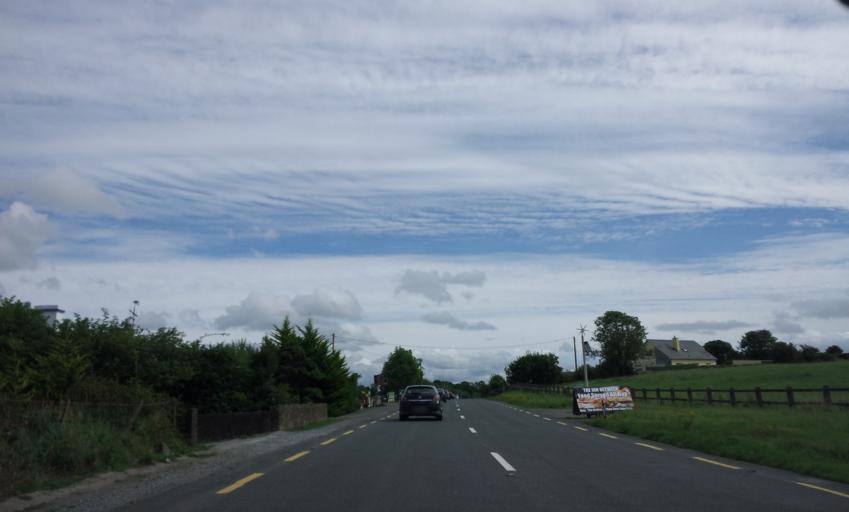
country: IE
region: Munster
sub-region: Ciarrai
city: Cill Airne
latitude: 52.0751
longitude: -9.6219
